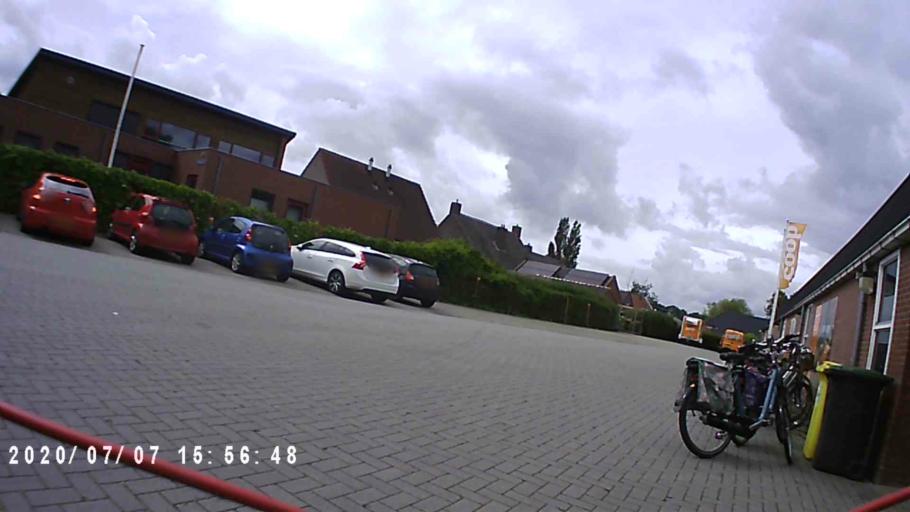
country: NL
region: Groningen
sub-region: Gemeente Winsum
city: Winsum
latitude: 53.3636
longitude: 6.5141
